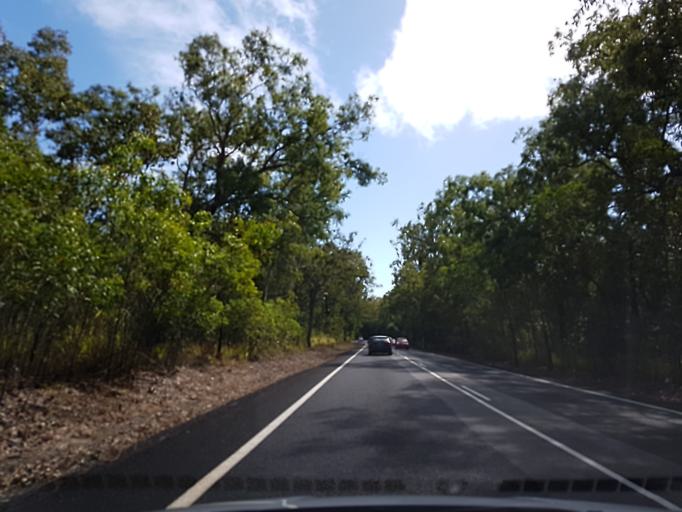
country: AU
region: Queensland
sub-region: Cairns
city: Palm Cove
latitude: -16.6692
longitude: 145.5680
